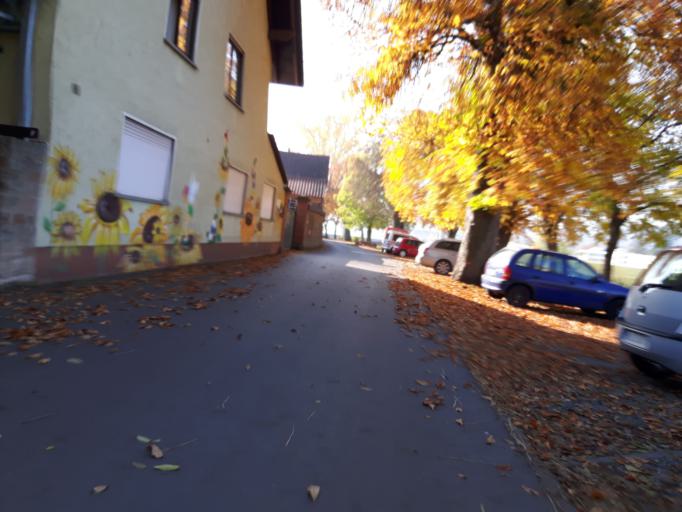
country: DE
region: Bavaria
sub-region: Regierungsbezirk Unterfranken
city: Kleinwallstadt
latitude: 49.8725
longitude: 9.1626
